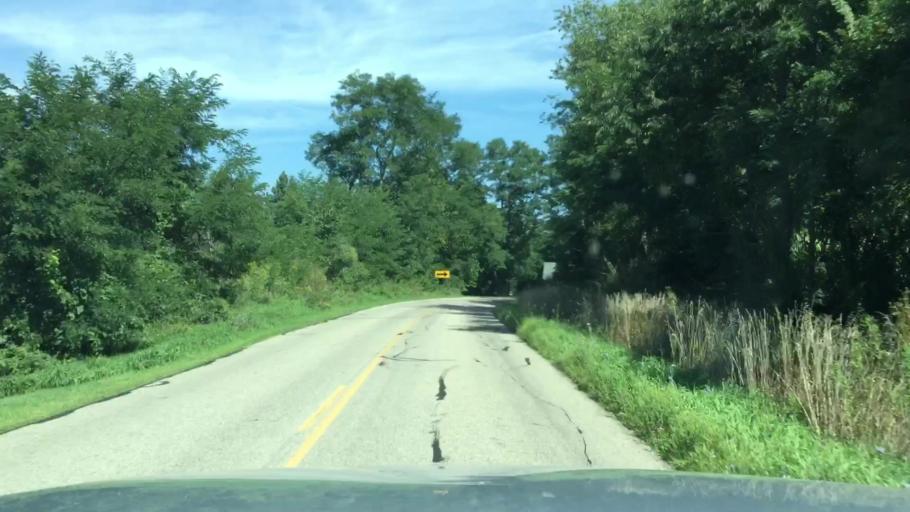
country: US
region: Michigan
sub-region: Lenawee County
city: Manitou Beach-Devils Lake
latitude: 42.0073
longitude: -84.3203
